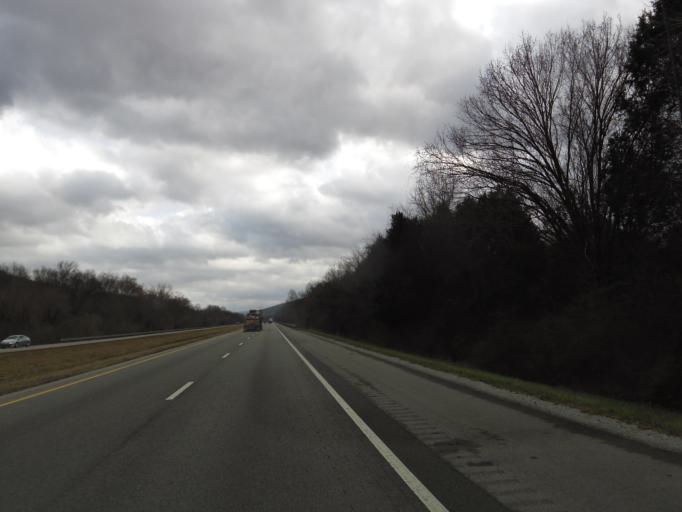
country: US
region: Tennessee
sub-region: Marion County
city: South Pittsburg
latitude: 35.0703
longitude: -85.7333
